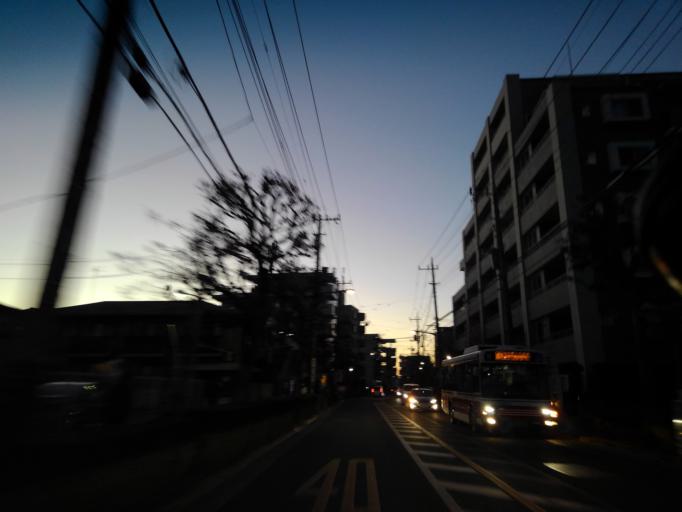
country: JP
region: Tokyo
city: Chofugaoka
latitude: 35.6454
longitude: 139.5556
